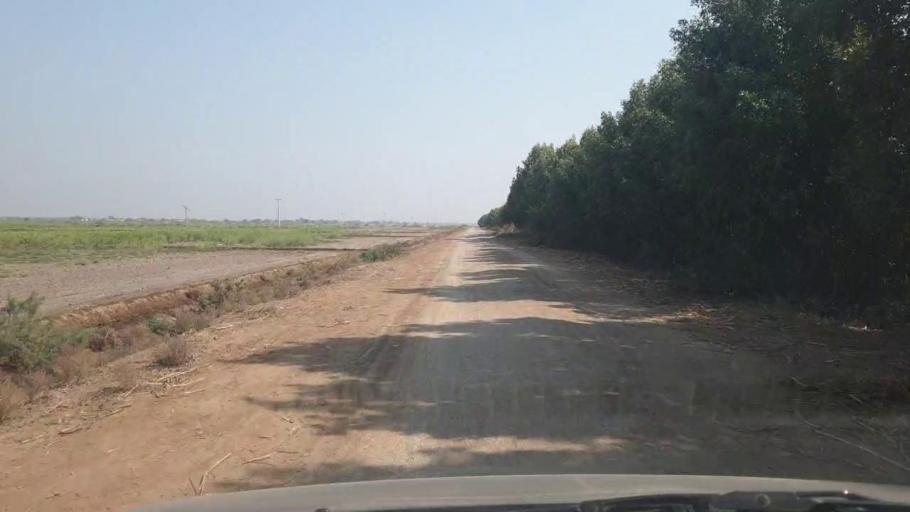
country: PK
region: Sindh
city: Digri
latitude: 25.2345
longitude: 69.1557
